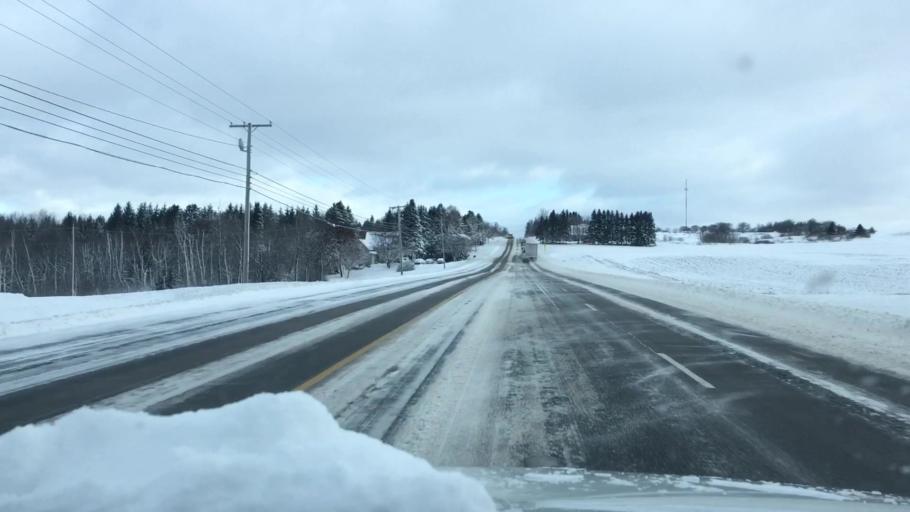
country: US
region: Maine
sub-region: Aroostook County
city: Presque Isle
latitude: 46.7203
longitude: -68.0068
